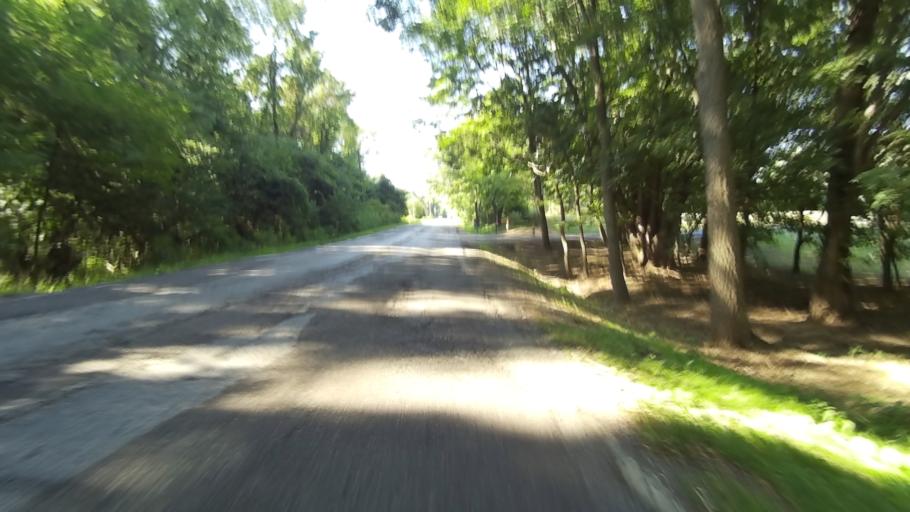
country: US
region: Ohio
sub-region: Portage County
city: Streetsboro
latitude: 41.2319
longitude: -81.3085
